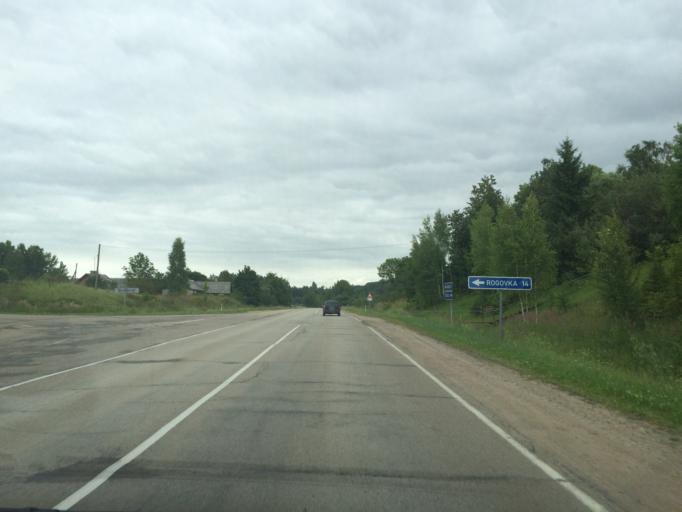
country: LV
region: Rezekne
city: Rezekne
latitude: 56.5859
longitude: 27.4007
